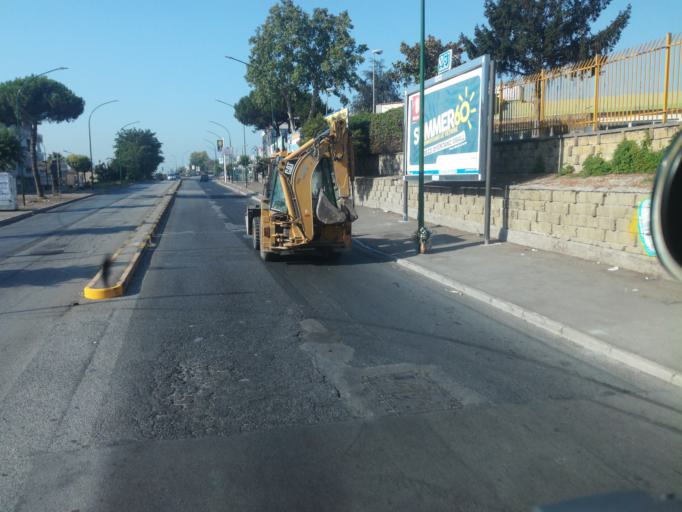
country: IT
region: Campania
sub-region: Provincia di Napoli
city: Arpino
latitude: 40.8860
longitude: 14.3205
